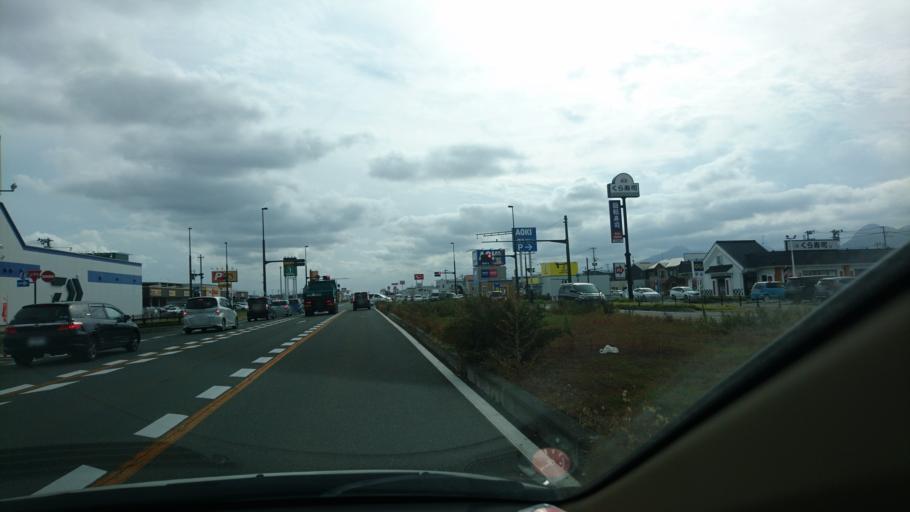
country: JP
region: Iwate
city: Morioka-shi
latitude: 39.6777
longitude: 141.1353
